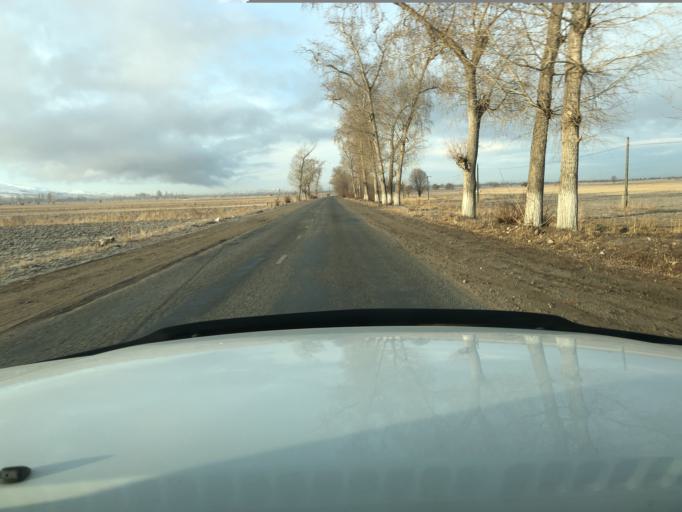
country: KG
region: Ysyk-Koel
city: Karakol
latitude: 42.4762
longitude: 78.3230
